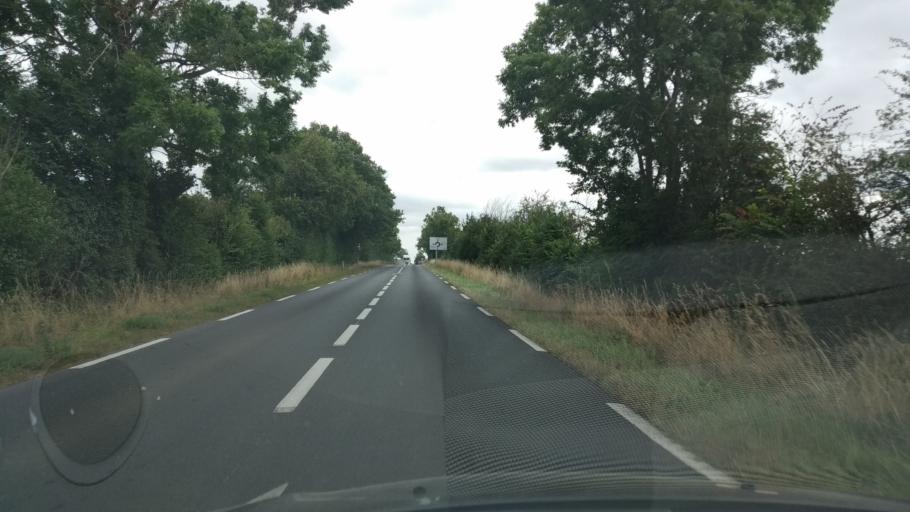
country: FR
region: Poitou-Charentes
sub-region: Departement de la Vienne
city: Roches-Premarie-Andille
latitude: 46.4978
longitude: 0.3648
